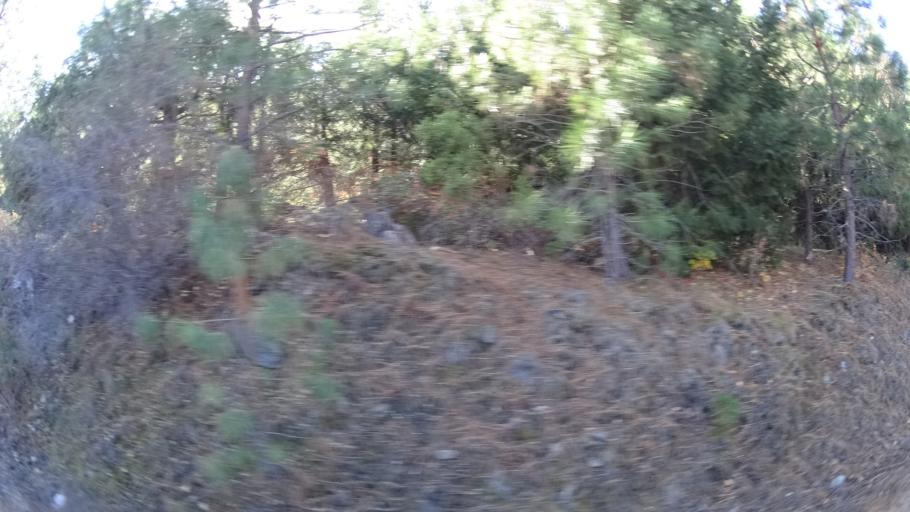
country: US
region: California
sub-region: Siskiyou County
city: Yreka
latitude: 41.8348
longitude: -122.8577
